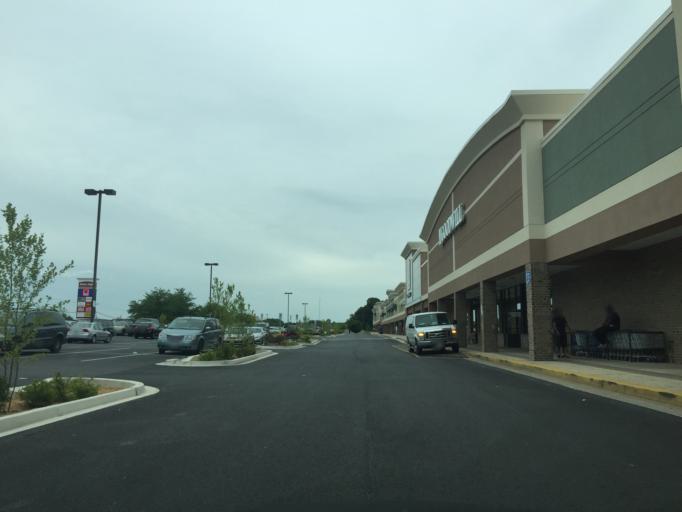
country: US
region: Maryland
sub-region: Baltimore County
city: Perry Hall
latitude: 39.3945
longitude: -76.4865
